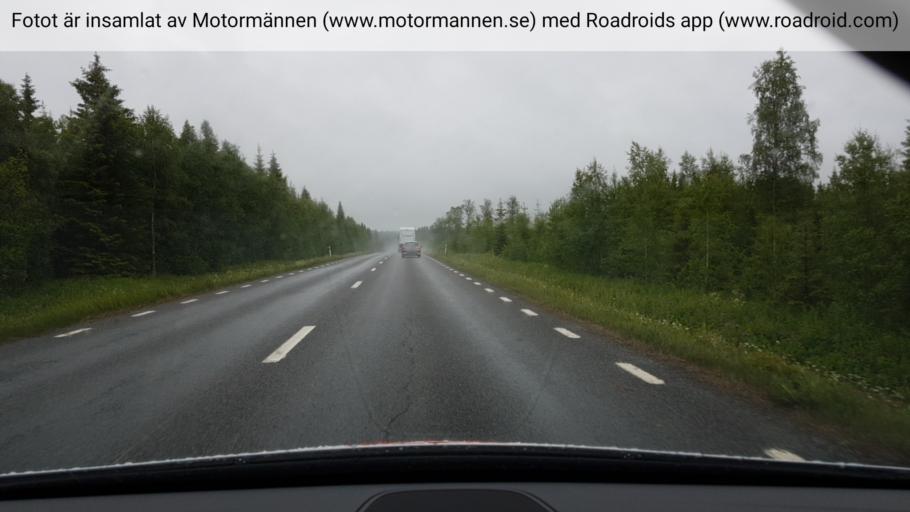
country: SE
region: Jaemtland
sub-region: OEstersunds Kommun
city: Lit
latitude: 63.4777
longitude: 15.2180
